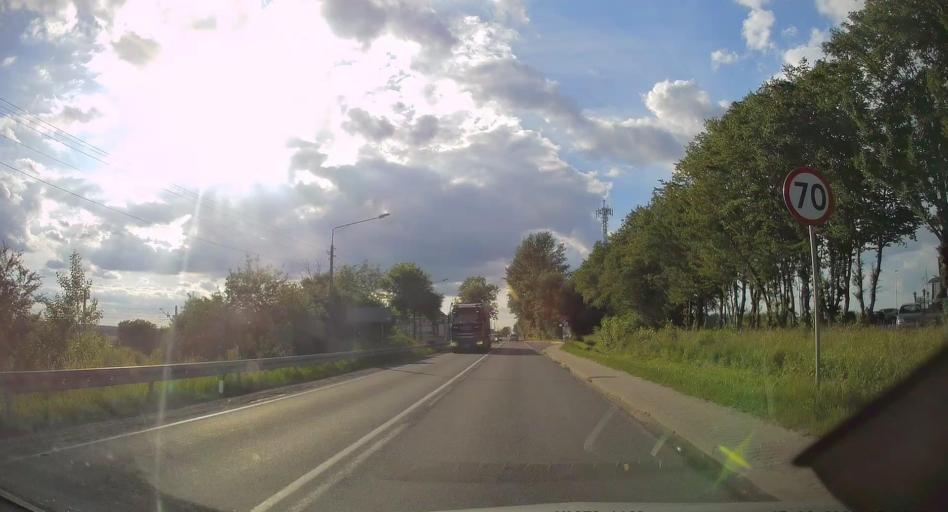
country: PL
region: Lesser Poland Voivodeship
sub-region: Powiat wadowicki
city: Roczyny
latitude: 49.8600
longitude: 19.3219
